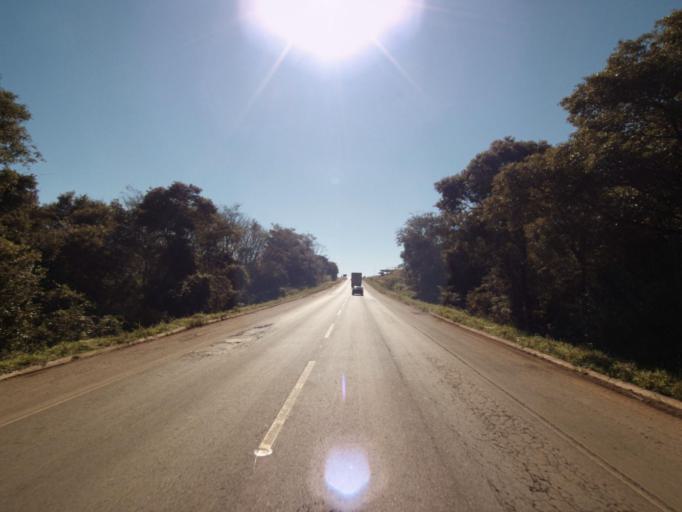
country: BR
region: Rio Grande do Sul
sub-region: Frederico Westphalen
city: Frederico Westphalen
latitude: -26.9104
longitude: -53.1876
